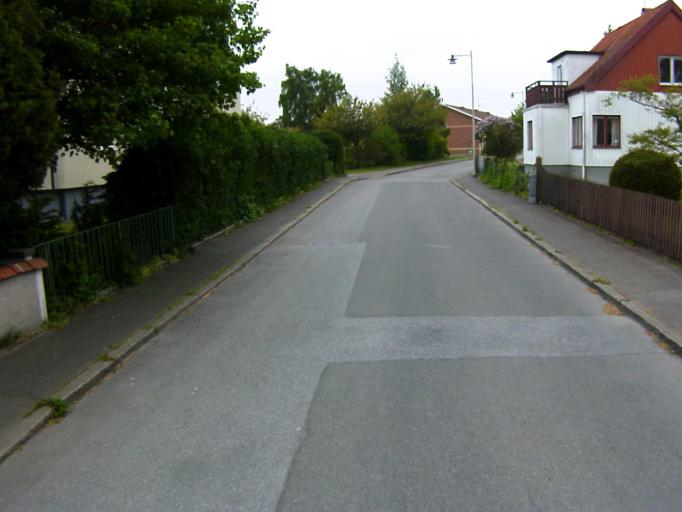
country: SE
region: Skane
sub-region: Kristianstads Kommun
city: Ahus
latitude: 55.9260
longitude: 14.2984
